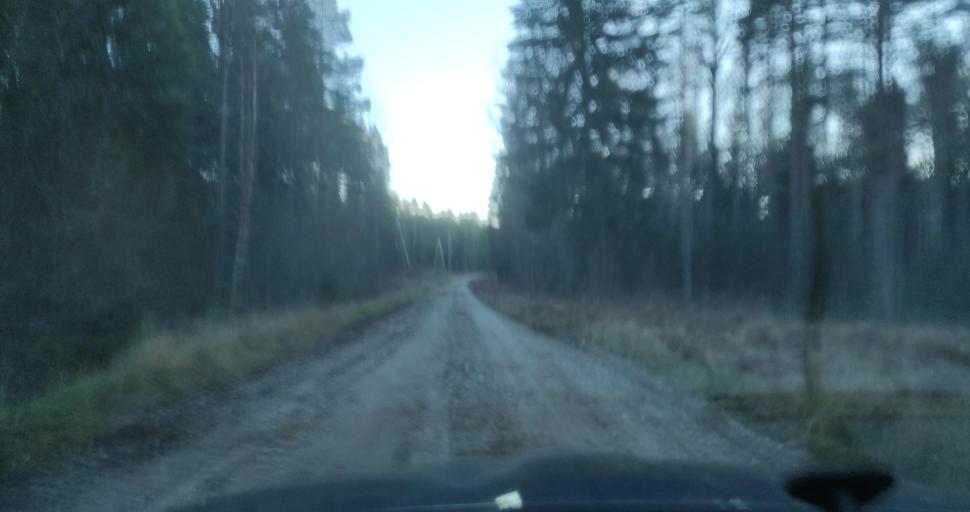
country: LV
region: Dundaga
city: Dundaga
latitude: 57.3803
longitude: 22.0817
